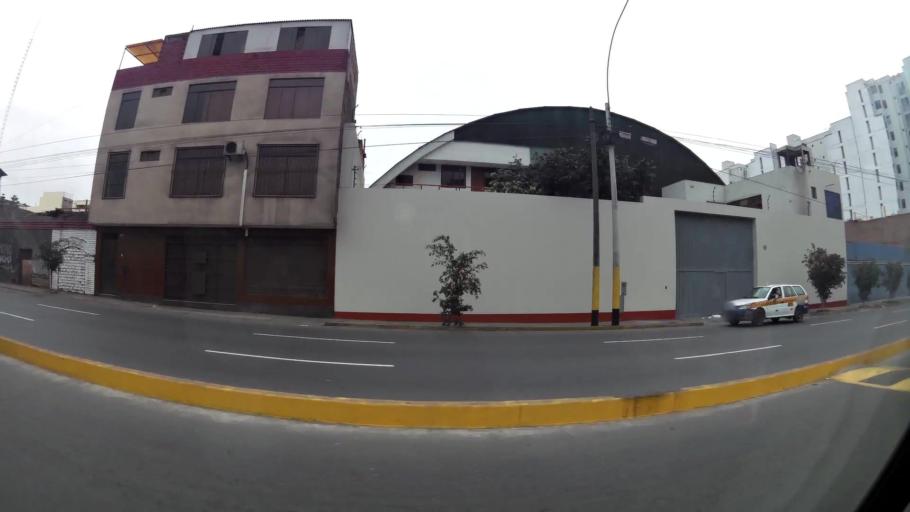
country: PE
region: Lima
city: Lima
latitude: -12.0500
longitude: -77.0488
